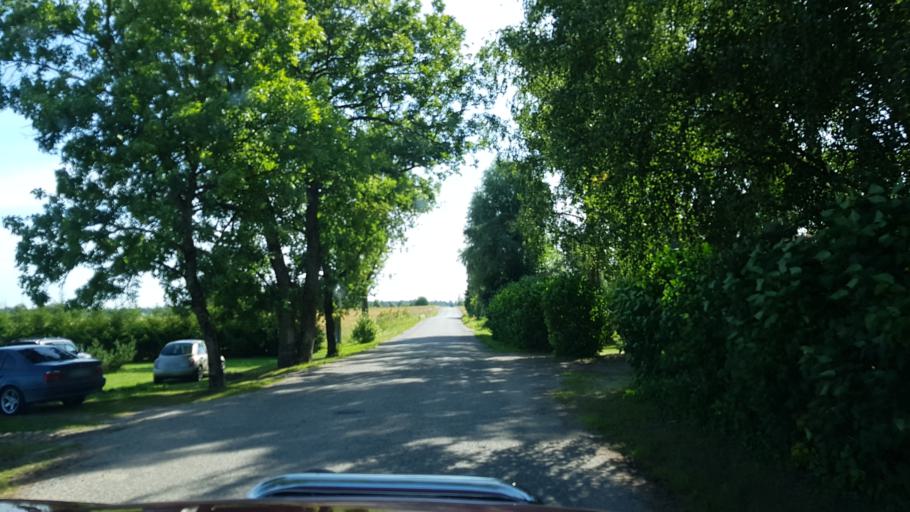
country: EE
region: Jaervamaa
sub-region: Jaerva-Jaani vald
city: Jarva-Jaani
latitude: 59.0889
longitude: 25.7310
